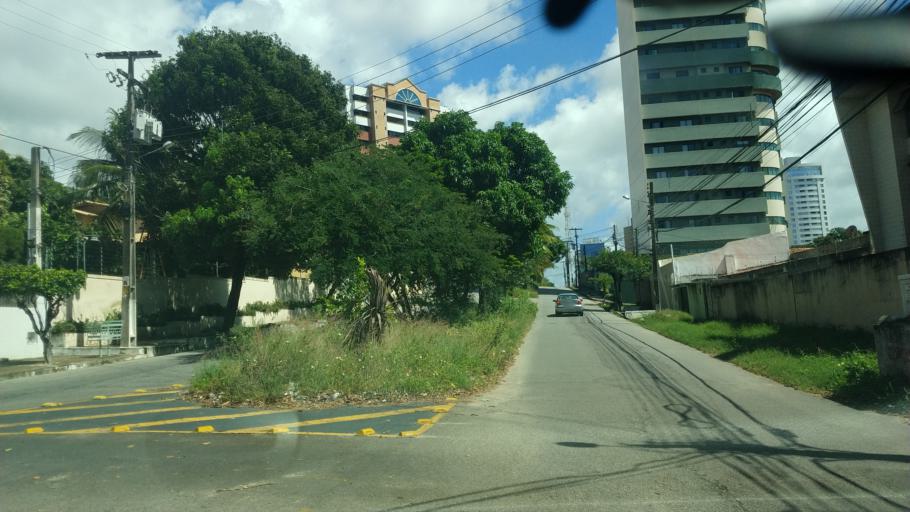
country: BR
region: Rio Grande do Norte
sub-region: Natal
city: Natal
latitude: -5.8308
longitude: -35.2195
